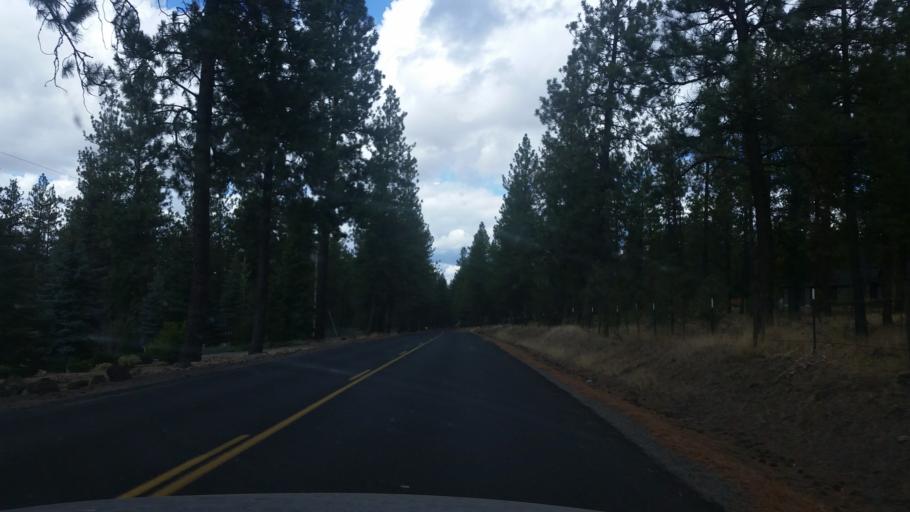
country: US
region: Washington
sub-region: Spokane County
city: Cheney
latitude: 47.5490
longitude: -117.4835
